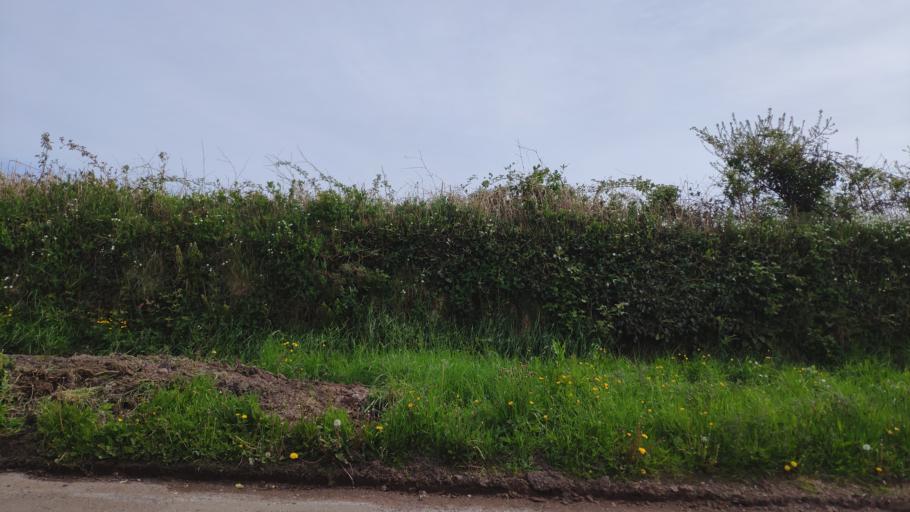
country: IE
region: Munster
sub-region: County Cork
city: Blarney
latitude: 51.9585
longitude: -8.5110
